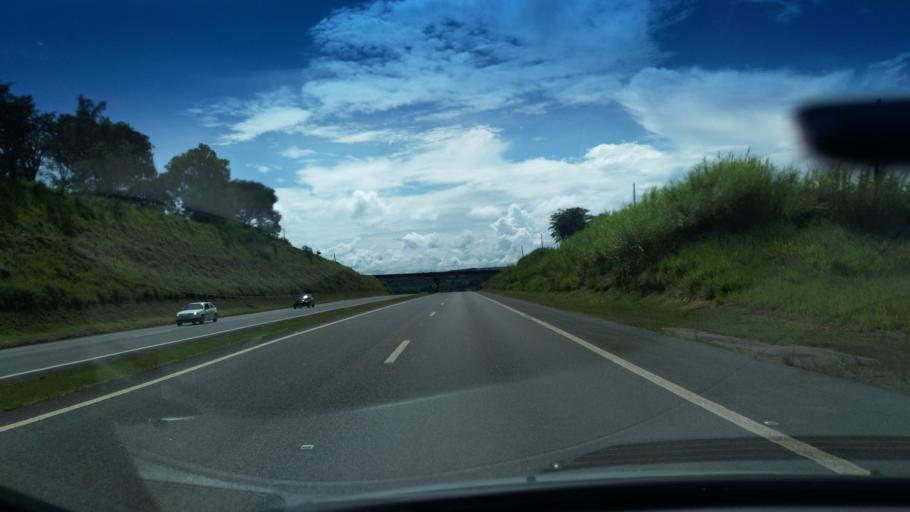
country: BR
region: Sao Paulo
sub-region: Santo Antonio Do Jardim
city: Espirito Santo do Pinhal
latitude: -22.2419
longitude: -46.8029
